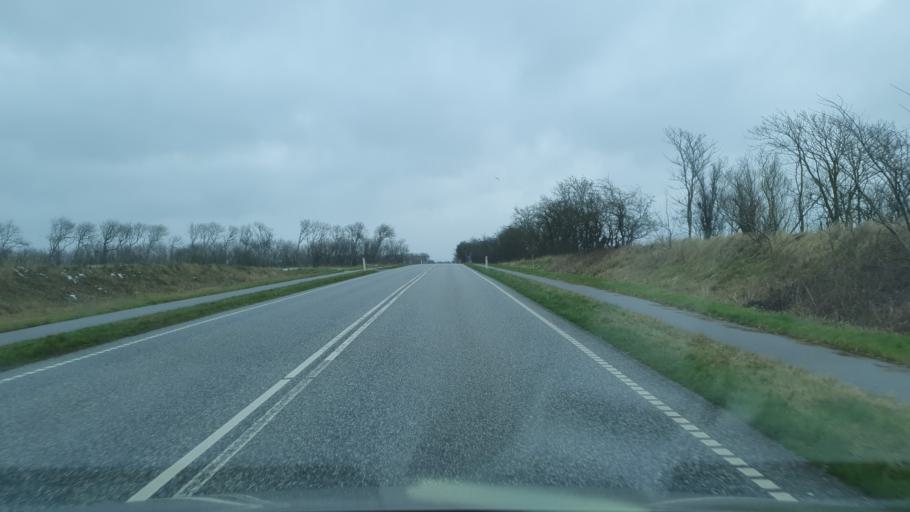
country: DK
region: North Denmark
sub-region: Jammerbugt Kommune
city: Fjerritslev
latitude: 57.0982
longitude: 9.1527
